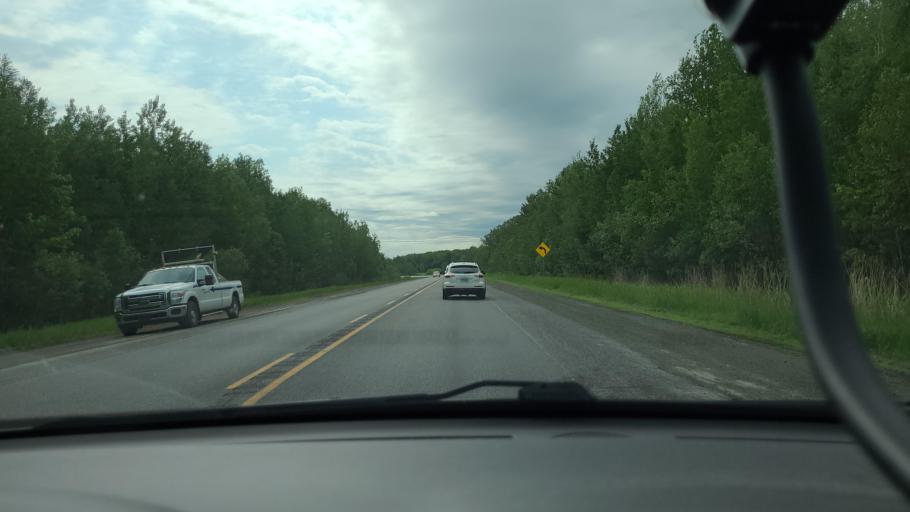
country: CA
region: Quebec
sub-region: Lanaudiere
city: Crabtree
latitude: 45.9626
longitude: -73.5141
